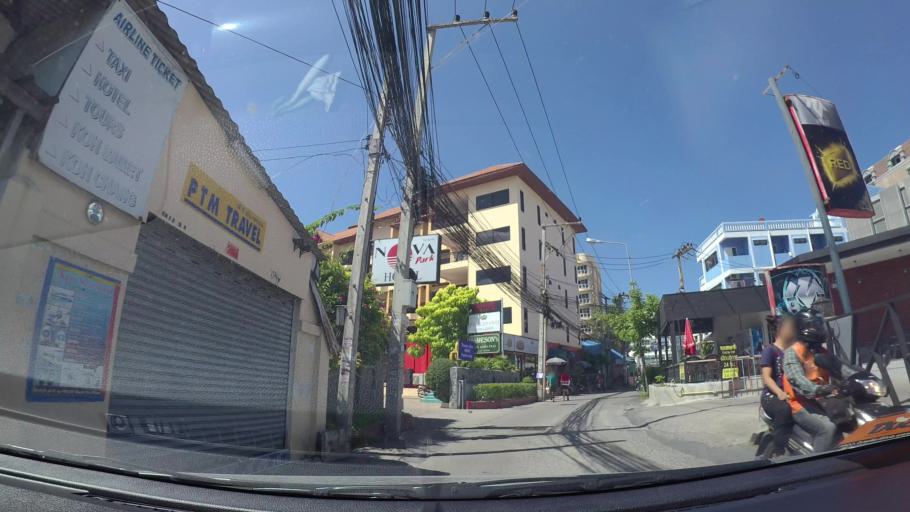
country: TH
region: Chon Buri
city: Phatthaya
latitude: 12.9406
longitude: 100.8908
